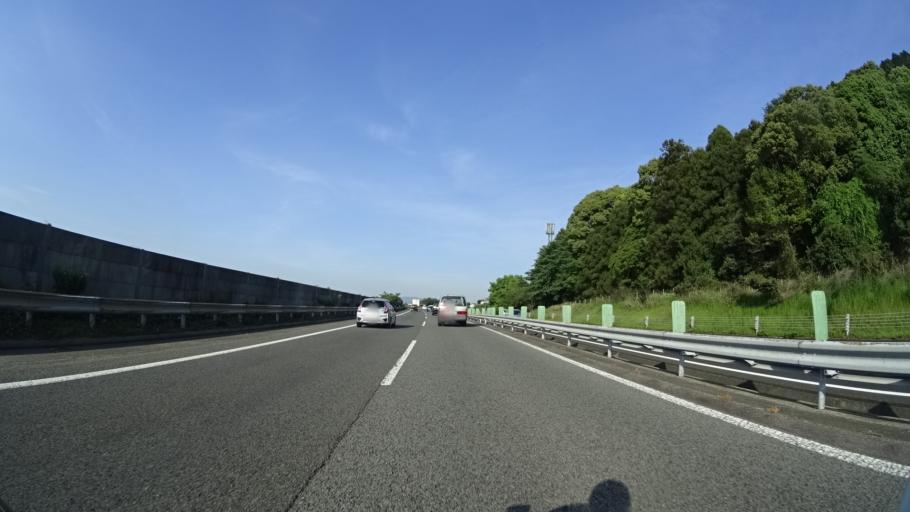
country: JP
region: Ehime
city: Kawanoecho
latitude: 33.9626
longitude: 133.5227
